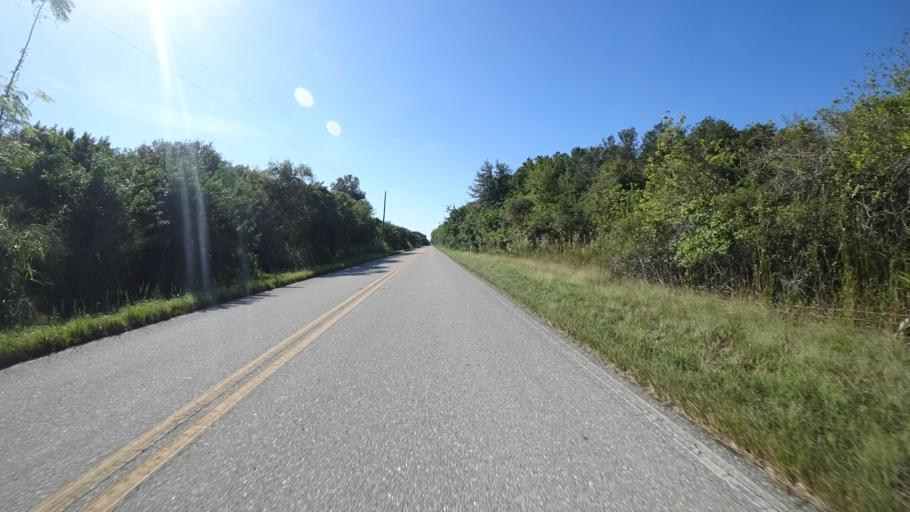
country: US
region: Florida
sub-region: Hillsborough County
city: Wimauma
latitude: 27.6327
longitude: -82.2925
